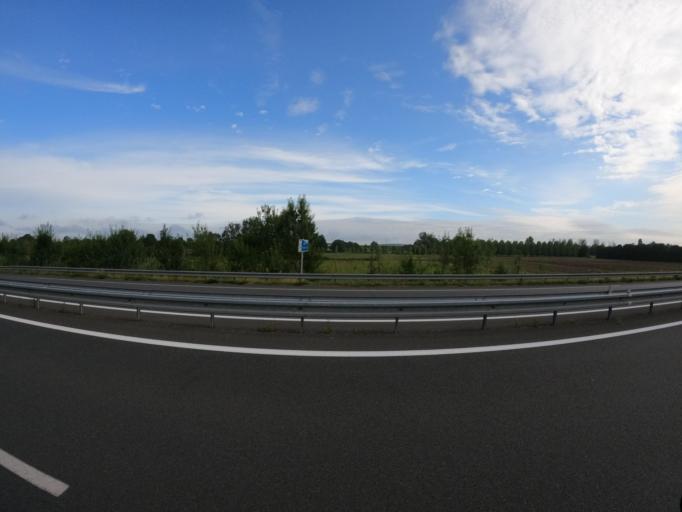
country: FR
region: Pays de la Loire
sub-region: Departement de Maine-et-Loire
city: Brain-sur-Allonnes
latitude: 47.2761
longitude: 0.0882
